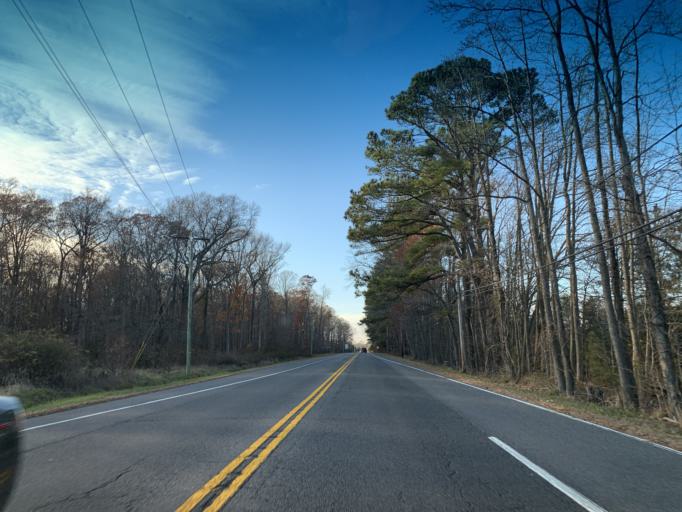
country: US
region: Maryland
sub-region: Queen Anne's County
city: Kingstown
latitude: 39.2012
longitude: -76.0449
